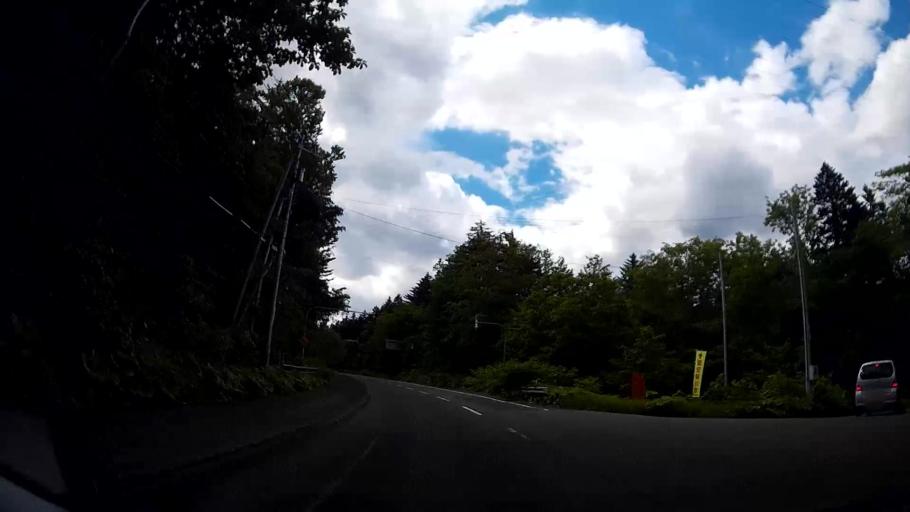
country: JP
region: Hokkaido
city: Kitahiroshima
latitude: 42.8448
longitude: 141.4605
